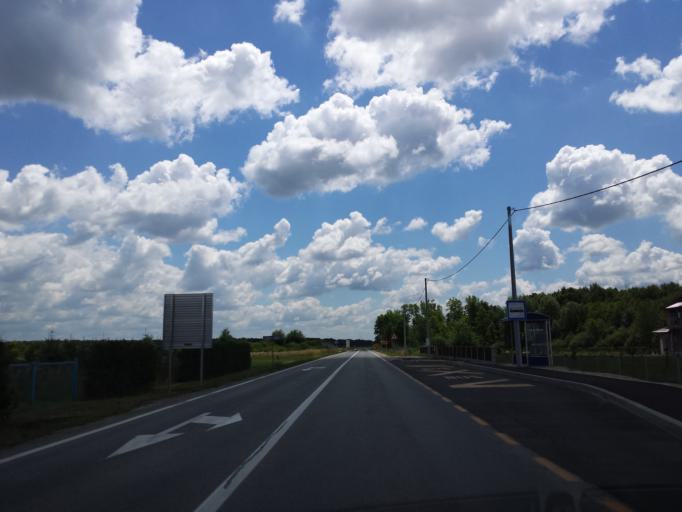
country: HR
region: Sisacko-Moslavacka
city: Lekenik
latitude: 45.5697
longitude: 16.2250
